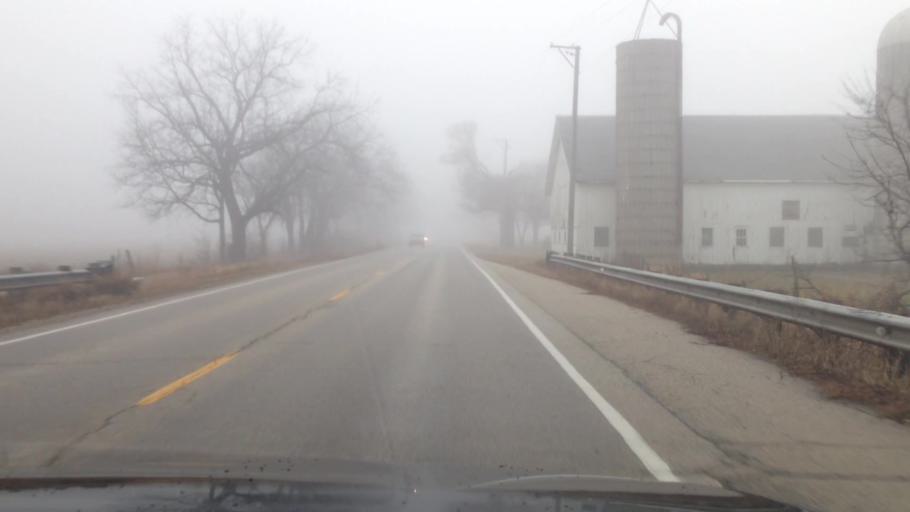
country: US
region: Illinois
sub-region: McHenry County
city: Hebron
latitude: 42.4083
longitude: -88.4381
